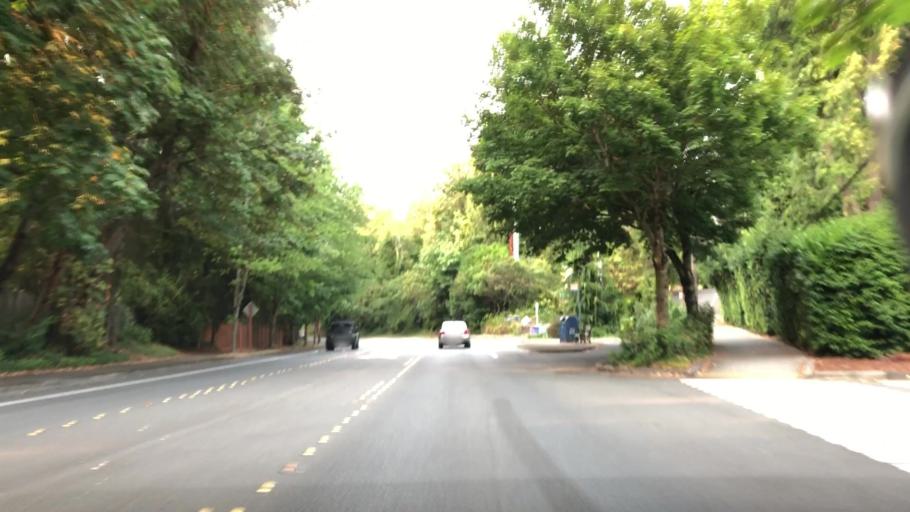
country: US
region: Washington
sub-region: King County
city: Mercer Island
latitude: 47.5558
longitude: -122.2212
